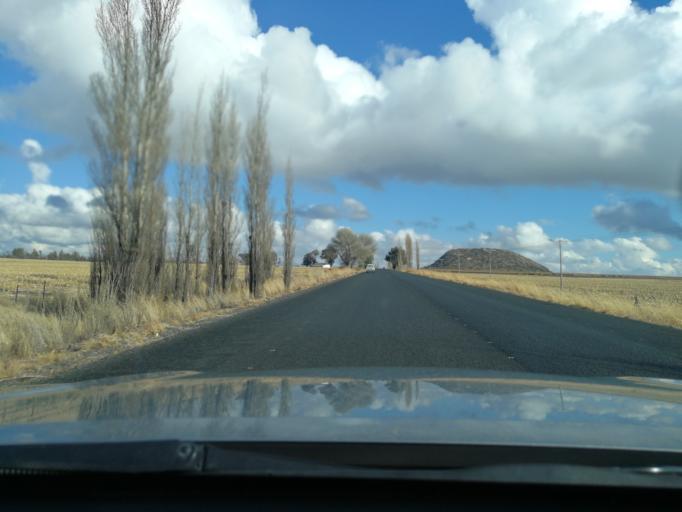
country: ZA
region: Orange Free State
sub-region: Thabo Mofutsanyana District Municipality
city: Reitz
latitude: -27.8900
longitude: 28.3973
